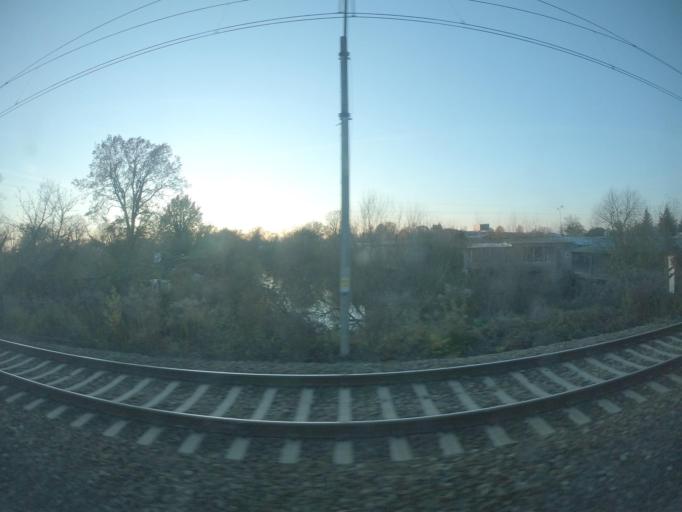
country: PL
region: Lubusz
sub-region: Powiat gorzowski
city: Kostrzyn nad Odra
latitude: 52.5777
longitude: 14.6436
